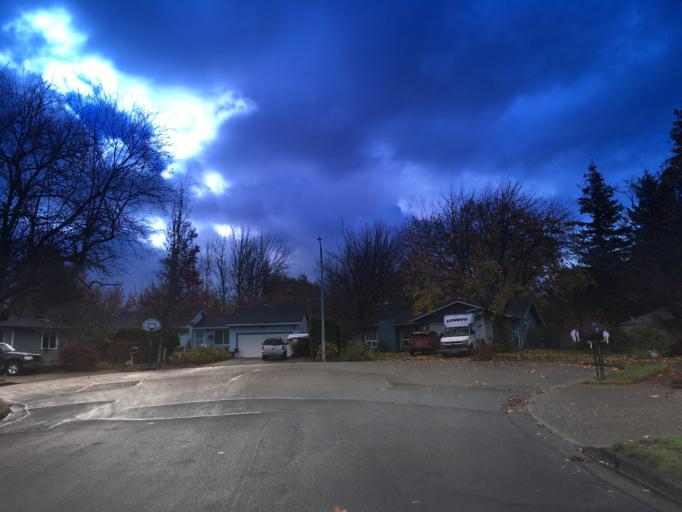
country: US
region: Oregon
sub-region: Multnomah County
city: Troutdale
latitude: 45.5198
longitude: -122.3786
